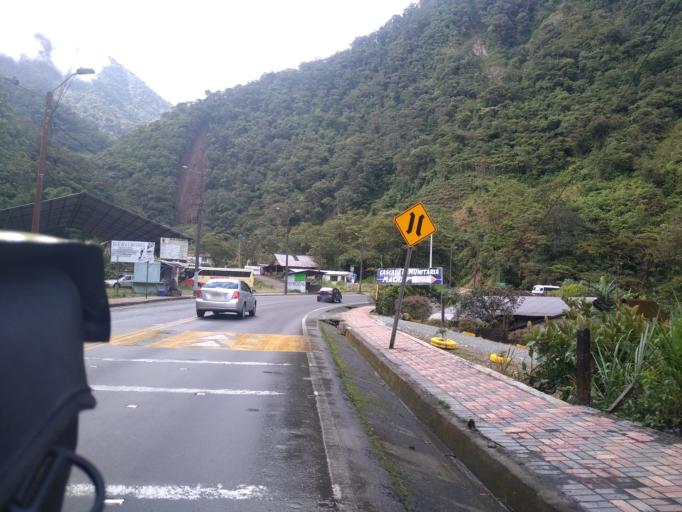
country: EC
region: Tungurahua
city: Banos
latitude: -1.4012
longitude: -78.2825
